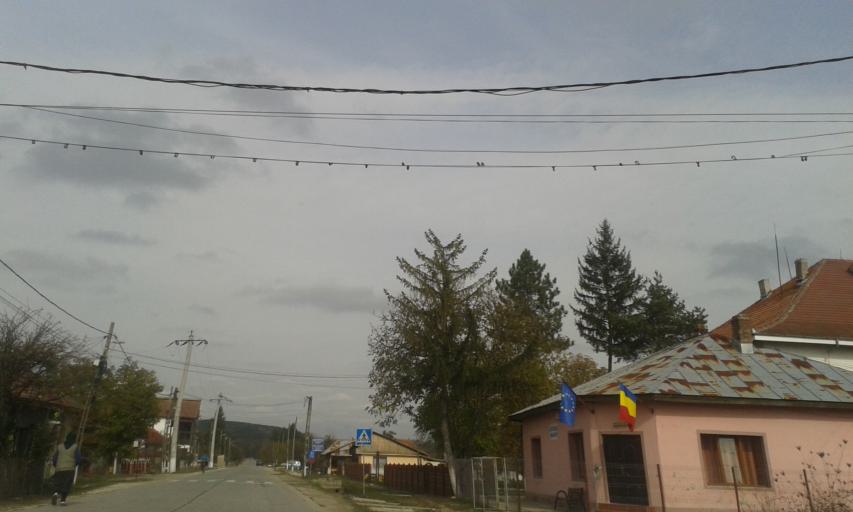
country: RO
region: Gorj
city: Logresti
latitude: 44.8736
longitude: 23.7069
